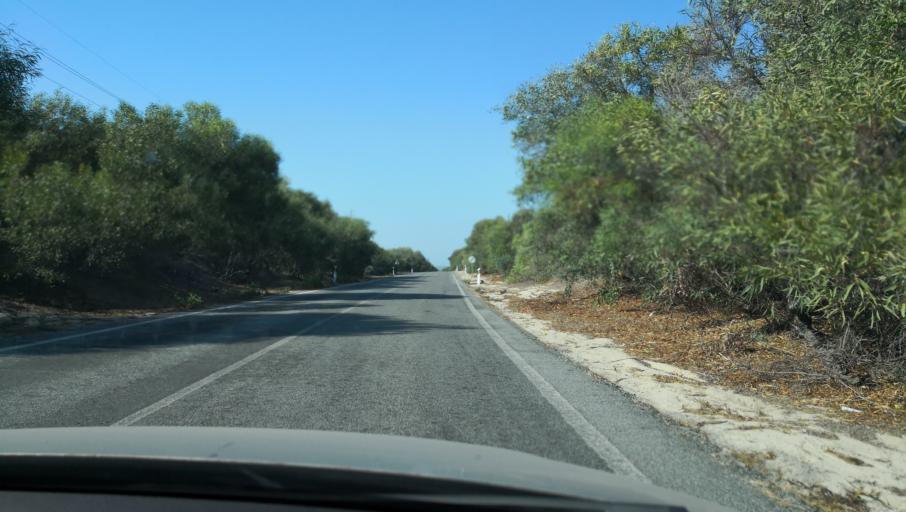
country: PT
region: Setubal
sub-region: Setubal
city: Setubal
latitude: 38.4128
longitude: -8.8146
